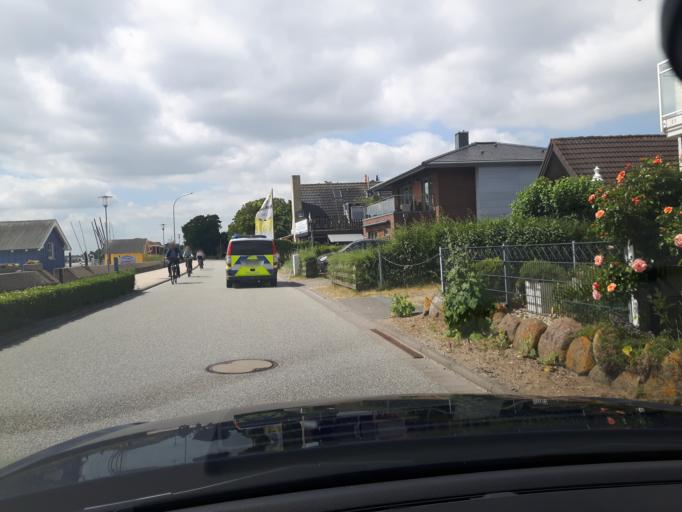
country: DE
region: Schleswig-Holstein
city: Sierksdorf
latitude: 54.0621
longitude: 10.7642
